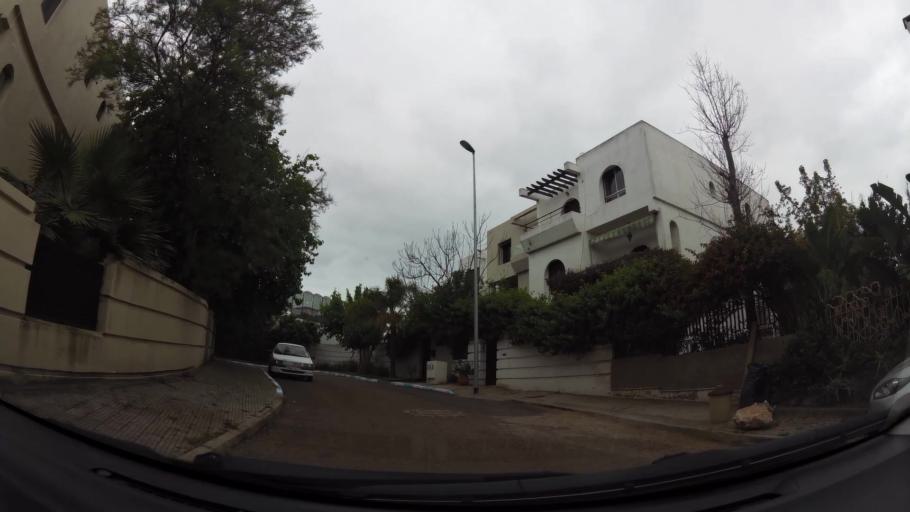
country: MA
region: Grand Casablanca
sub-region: Casablanca
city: Casablanca
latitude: 33.5977
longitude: -7.6584
